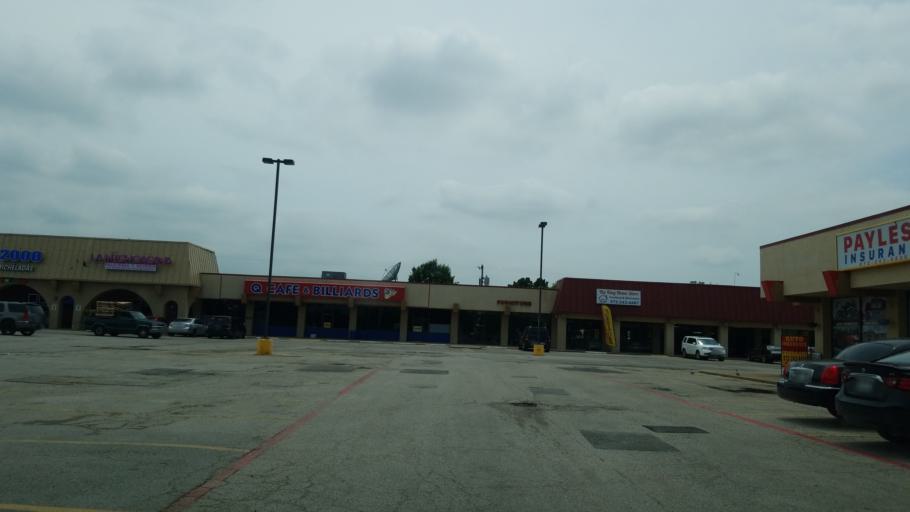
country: US
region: Texas
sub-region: Dallas County
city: Farmers Branch
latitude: 32.9092
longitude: -96.8739
